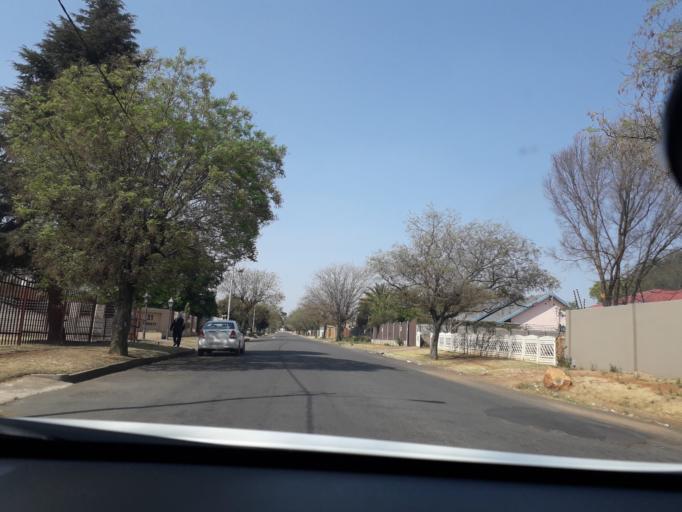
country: ZA
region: Gauteng
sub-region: City of Johannesburg Metropolitan Municipality
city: Modderfontein
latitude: -26.0939
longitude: 28.2255
